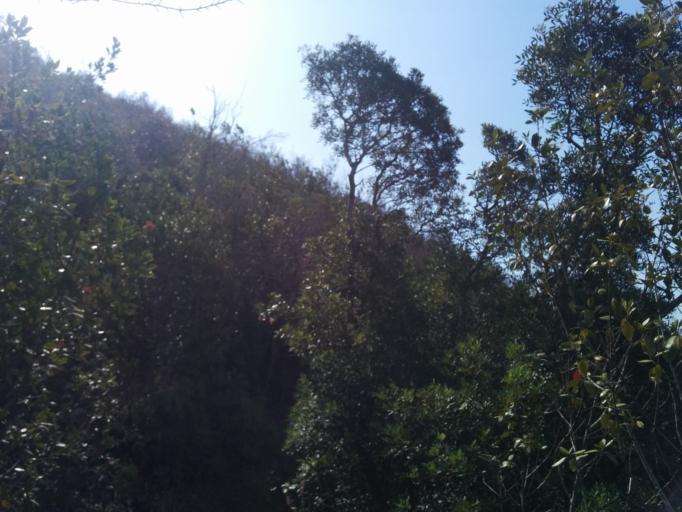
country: IT
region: Tuscany
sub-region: Provincia di Livorno
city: Portoferraio
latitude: 42.7535
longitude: 10.3145
